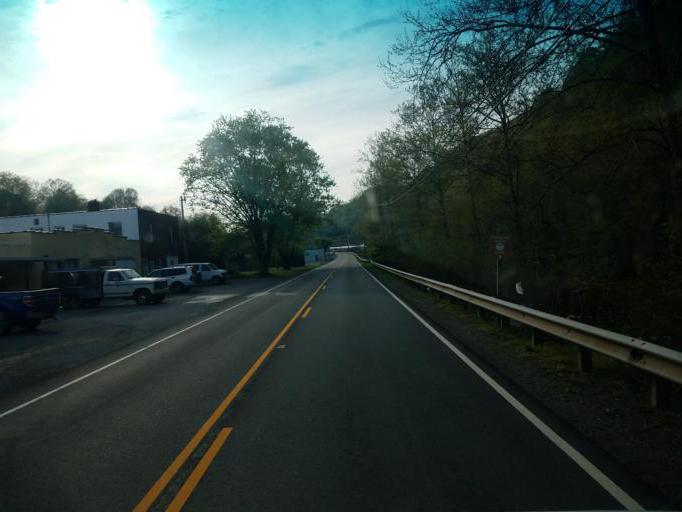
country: US
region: Virginia
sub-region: Smyth County
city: Marion
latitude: 36.8248
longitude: -81.5019
